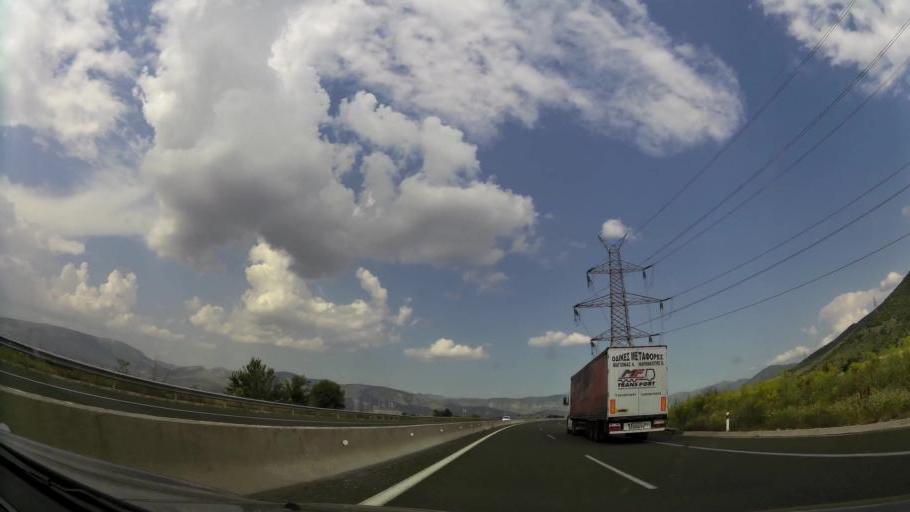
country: GR
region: West Macedonia
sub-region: Nomos Kozanis
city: Kleitos
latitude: 40.3698
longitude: 21.8766
